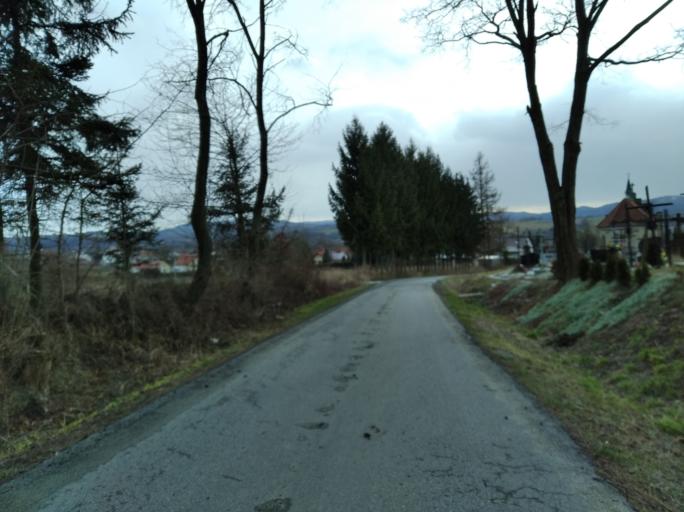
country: PL
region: Subcarpathian Voivodeship
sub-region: Powiat strzyzowski
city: Wysoka Strzyzowska
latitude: 49.8799
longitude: 21.7237
